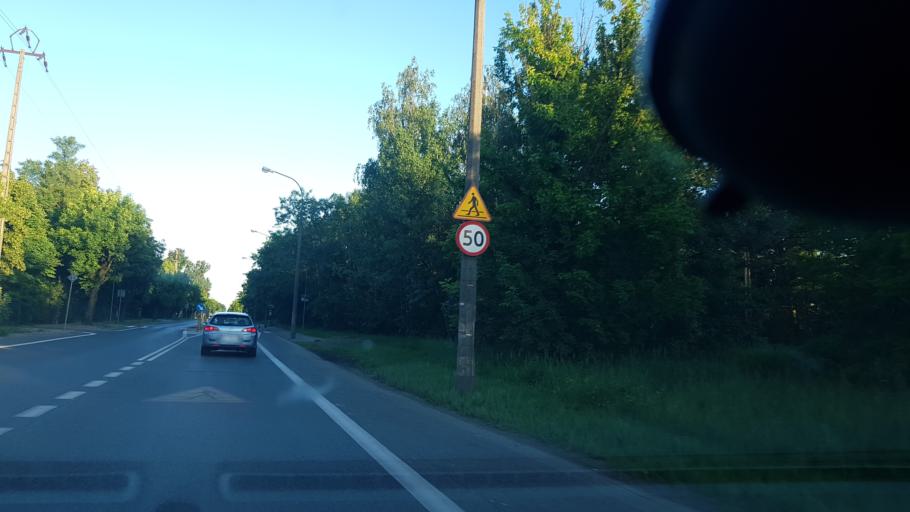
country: PL
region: Masovian Voivodeship
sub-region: Warszawa
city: Wawer
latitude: 52.1891
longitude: 21.1844
